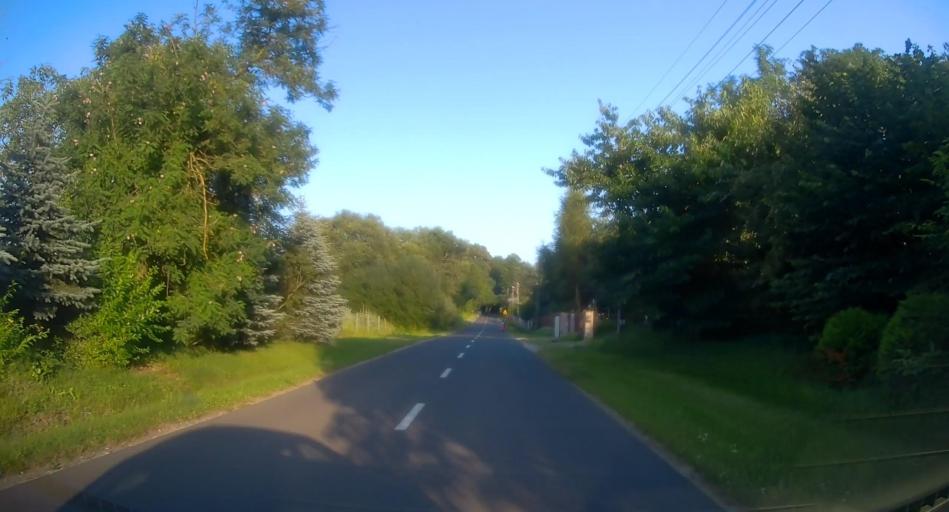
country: PL
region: Lodz Voivodeship
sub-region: Powiat skierniewicki
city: Kowiesy
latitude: 51.8926
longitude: 20.3855
